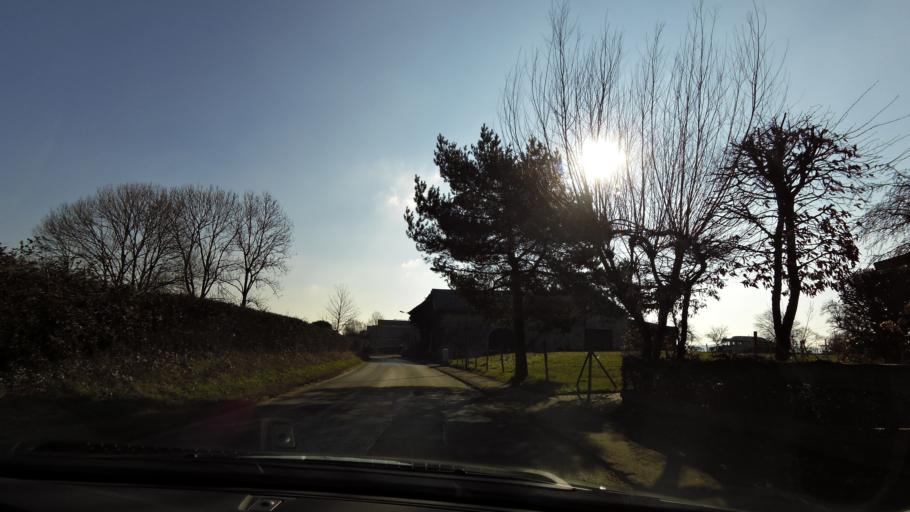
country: NL
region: Limburg
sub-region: Gemeente Vaals
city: Vaals
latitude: 50.7958
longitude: 5.9987
